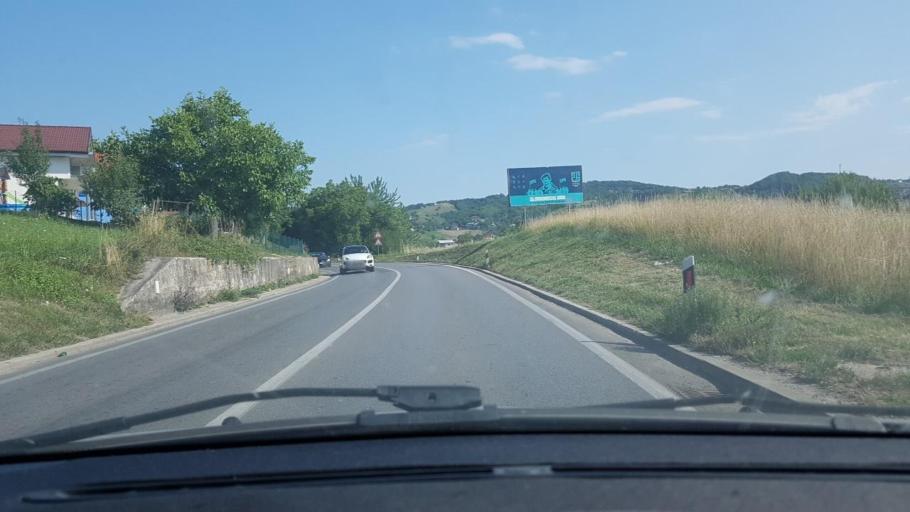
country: BA
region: Federation of Bosnia and Herzegovina
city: Cazin
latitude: 44.9625
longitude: 15.9277
